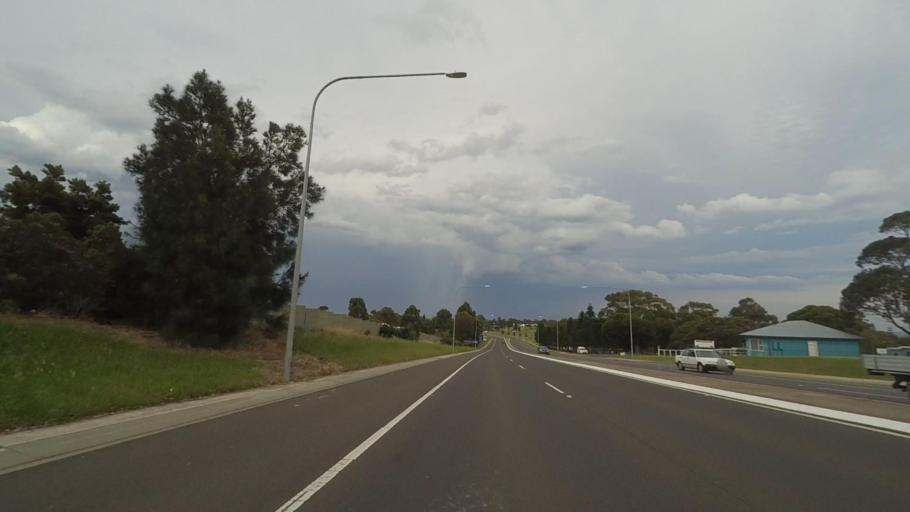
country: AU
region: New South Wales
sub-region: Shellharbour
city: Flinders
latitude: -34.5846
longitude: 150.8568
